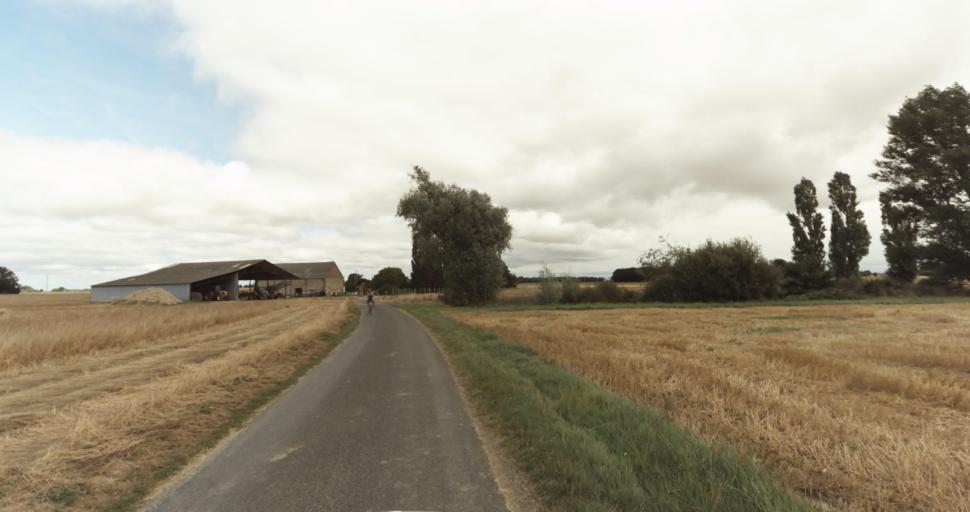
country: FR
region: Haute-Normandie
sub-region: Departement de l'Eure
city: La Madeleine-de-Nonancourt
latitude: 48.9019
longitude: 1.2047
